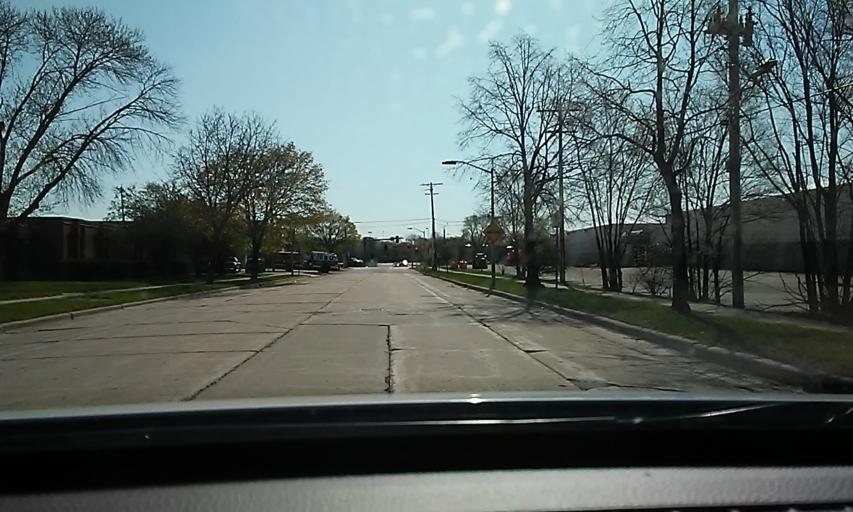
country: US
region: Wisconsin
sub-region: Waukesha County
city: Elm Grove
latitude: 43.0135
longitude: -88.0491
